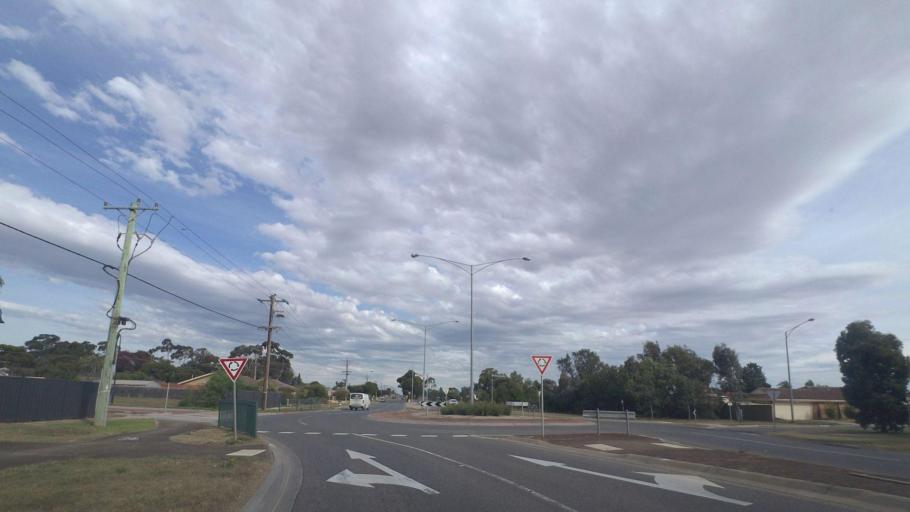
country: AU
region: Victoria
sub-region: Melton
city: Brookfield
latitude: -37.6988
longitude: 144.5655
